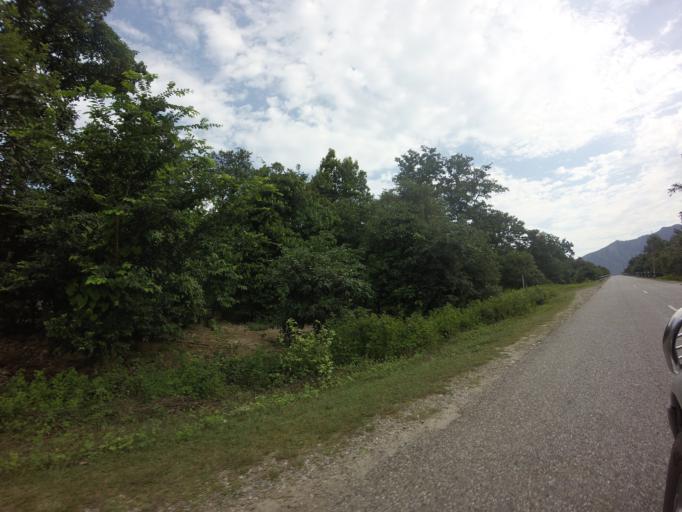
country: NP
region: Far Western
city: Tikapur
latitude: 28.6192
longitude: 81.2405
